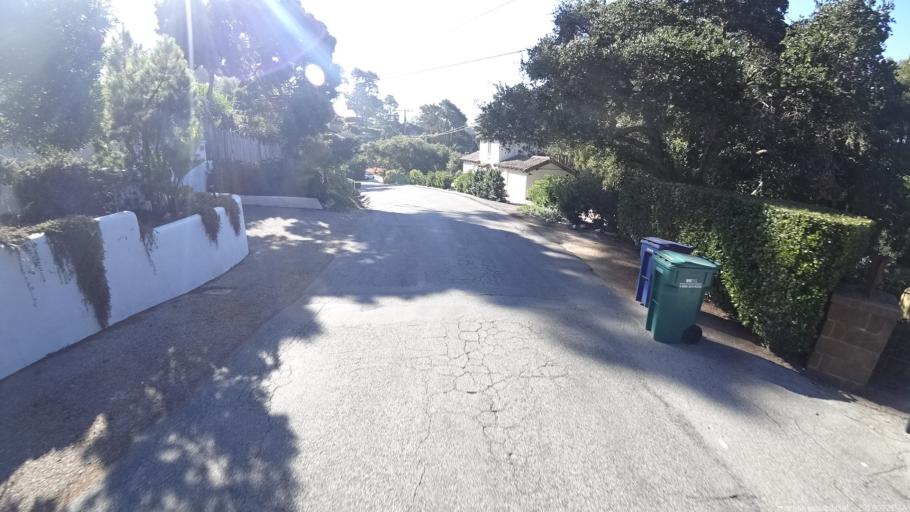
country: US
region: California
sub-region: Monterey County
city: Carmel-by-the-Sea
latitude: 36.5682
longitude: -121.9164
